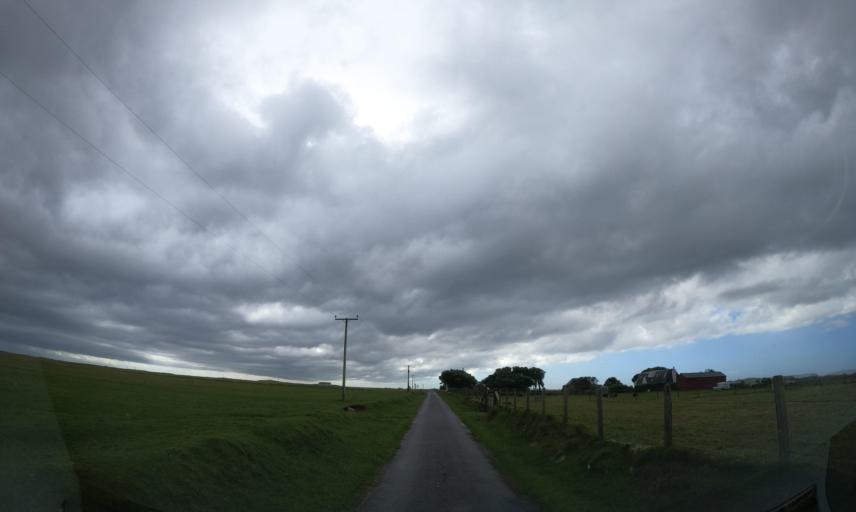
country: GB
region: Scotland
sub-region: Eilean Siar
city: Barra
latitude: 56.5330
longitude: -6.7983
